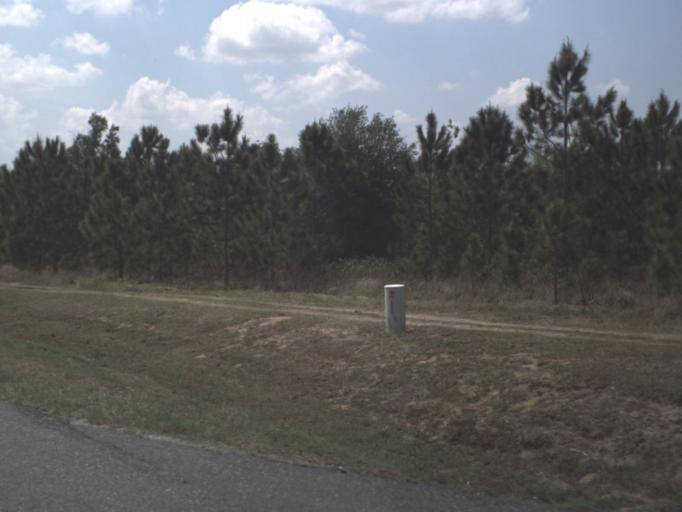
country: US
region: Florida
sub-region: Lake County
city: Howie In The Hills
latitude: 28.7057
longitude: -81.7725
